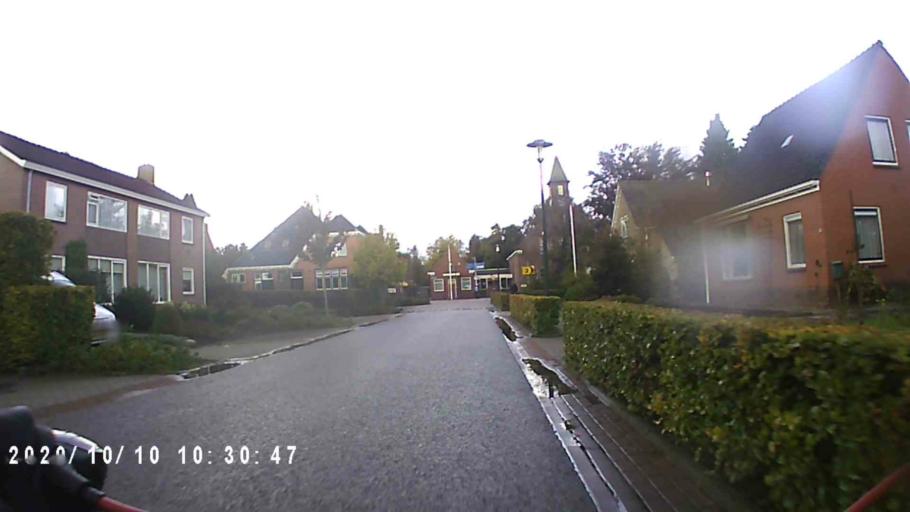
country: NL
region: Groningen
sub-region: Gemeente Leek
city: Leek
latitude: 53.1868
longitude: 6.3307
